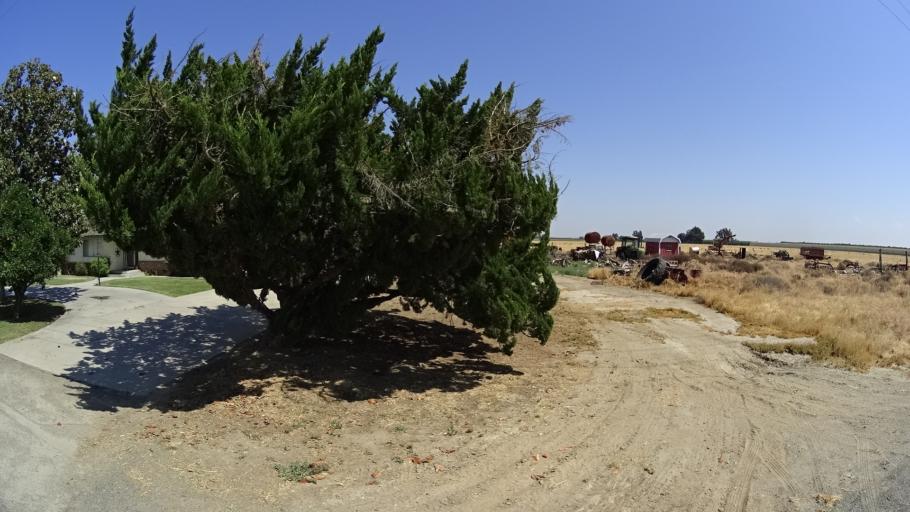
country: US
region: California
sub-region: Kings County
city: Lucerne
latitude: 36.3719
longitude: -119.6316
